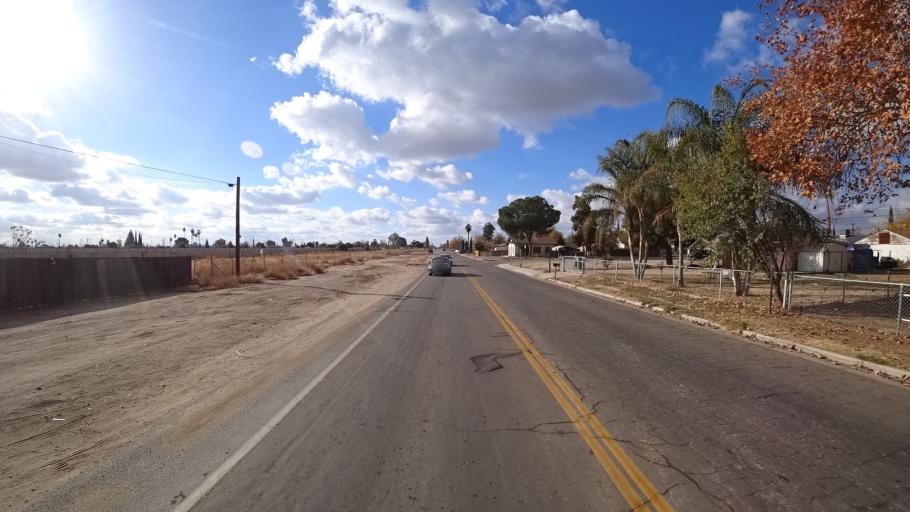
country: US
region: California
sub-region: Kern County
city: Bakersfield
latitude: 35.3322
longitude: -119.0050
